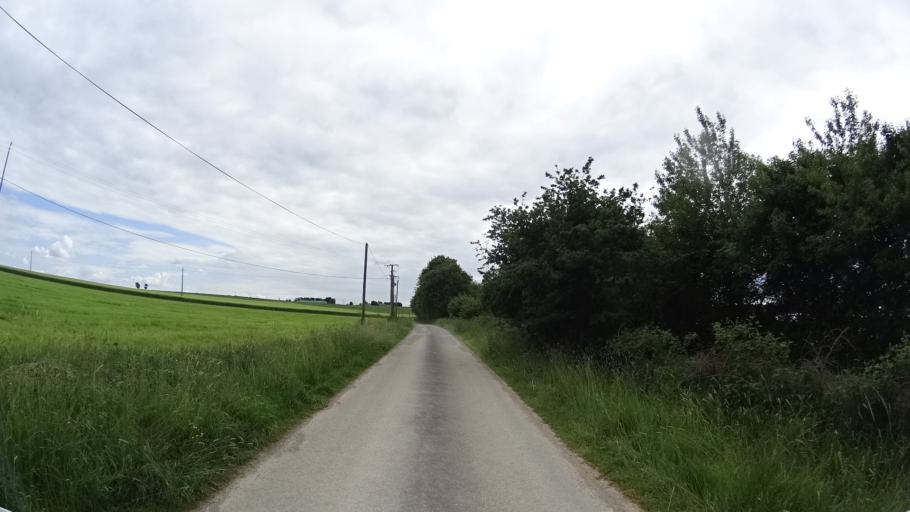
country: FR
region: Brittany
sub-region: Departement d'Ille-et-Vilaine
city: Monterfil
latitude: 48.0725
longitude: -2.0057
